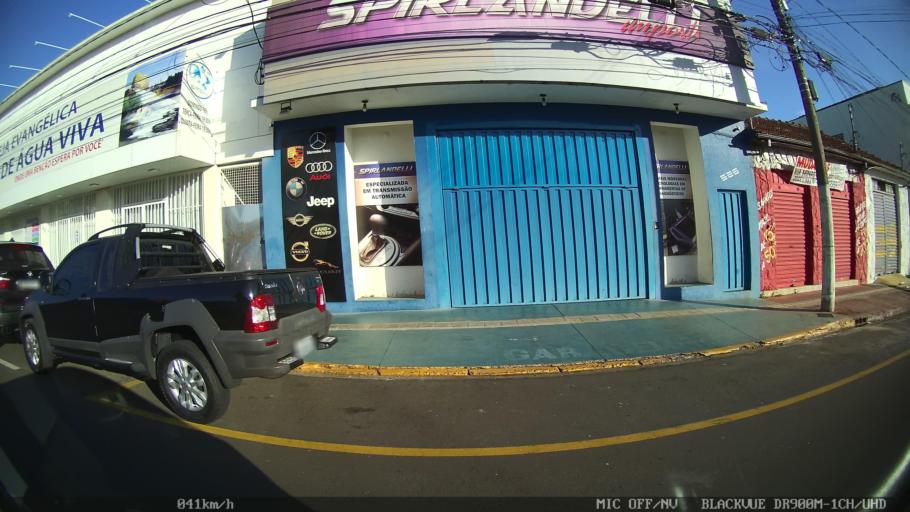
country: BR
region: Sao Paulo
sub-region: Franca
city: Franca
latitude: -20.5271
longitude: -47.3870
